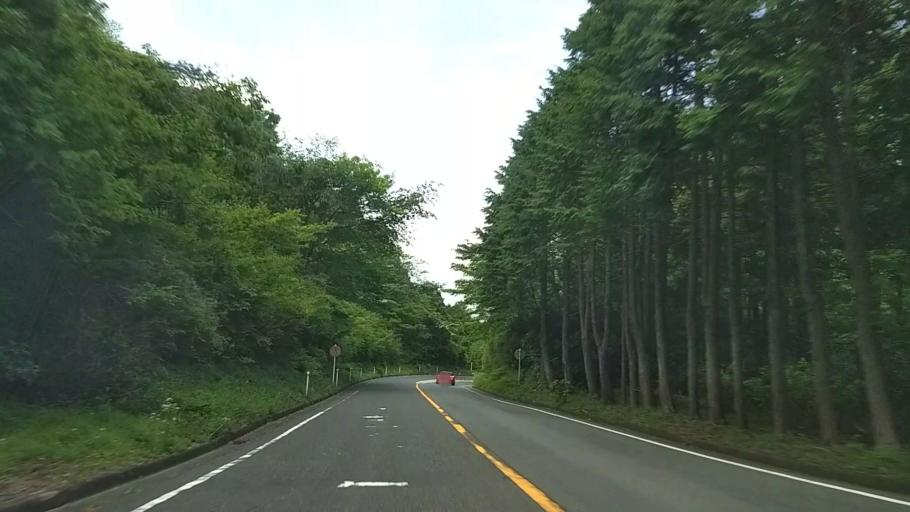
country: JP
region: Kanagawa
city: Odawara
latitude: 35.2160
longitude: 139.1117
